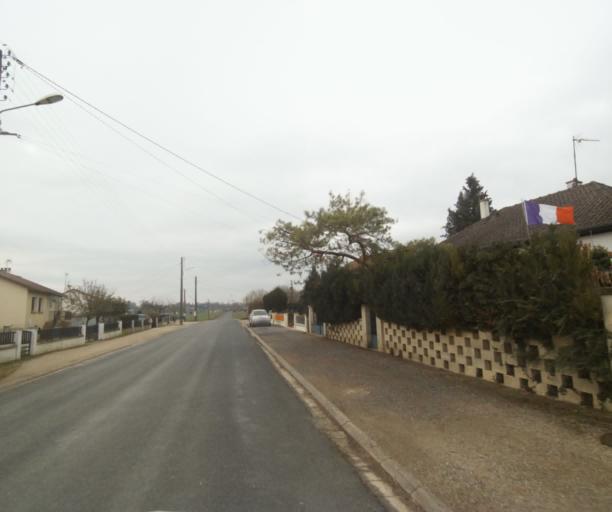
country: FR
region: Champagne-Ardenne
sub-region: Departement de la Haute-Marne
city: Villiers-en-Lieu
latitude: 48.6400
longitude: 4.8680
